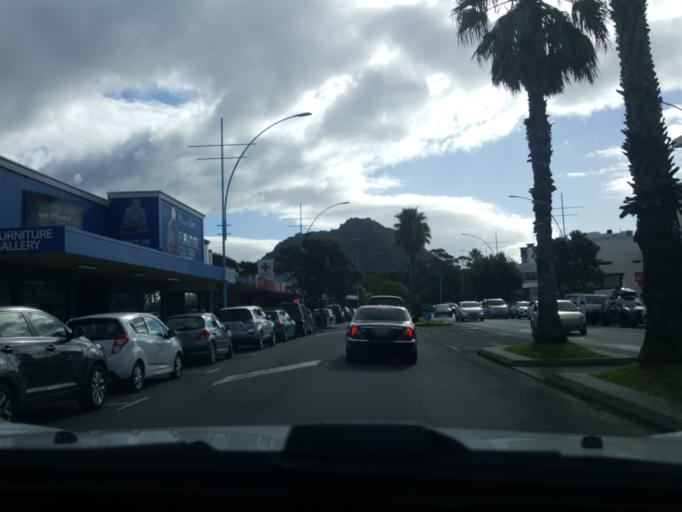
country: NZ
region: Bay of Plenty
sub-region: Tauranga City
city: Tauranga
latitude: -37.6420
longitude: 176.1856
